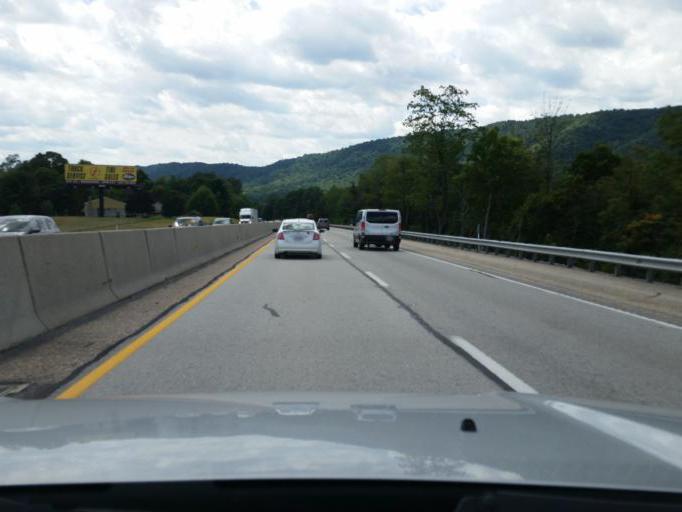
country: US
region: Pennsylvania
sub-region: Franklin County
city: Doylestown
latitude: 40.1588
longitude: -77.6987
